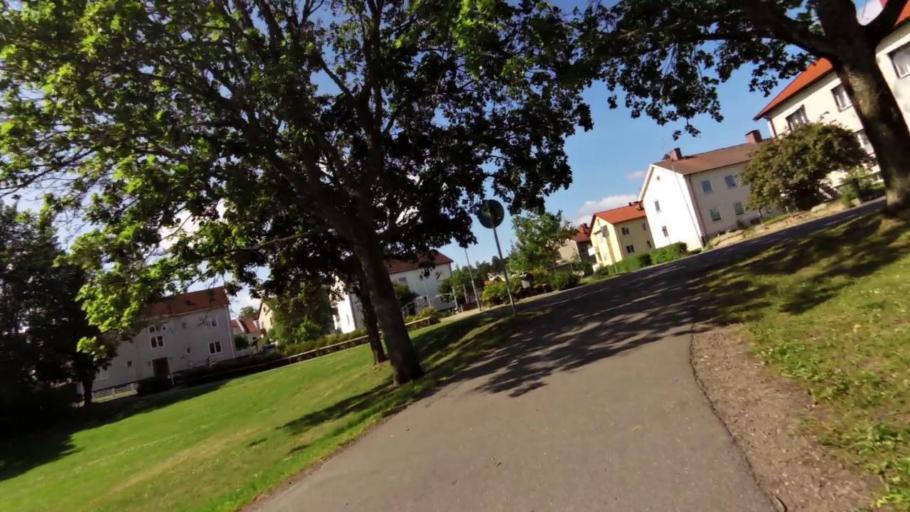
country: SE
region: OEstergoetland
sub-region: Linkopings Kommun
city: Linkoping
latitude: 58.3989
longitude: 15.6245
